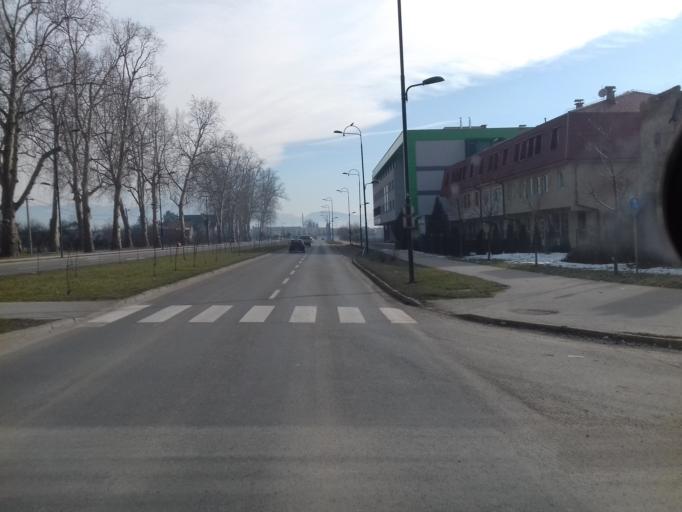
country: BA
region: Federation of Bosnia and Herzegovina
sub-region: Kanton Sarajevo
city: Sarajevo
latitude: 43.8270
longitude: 18.3161
